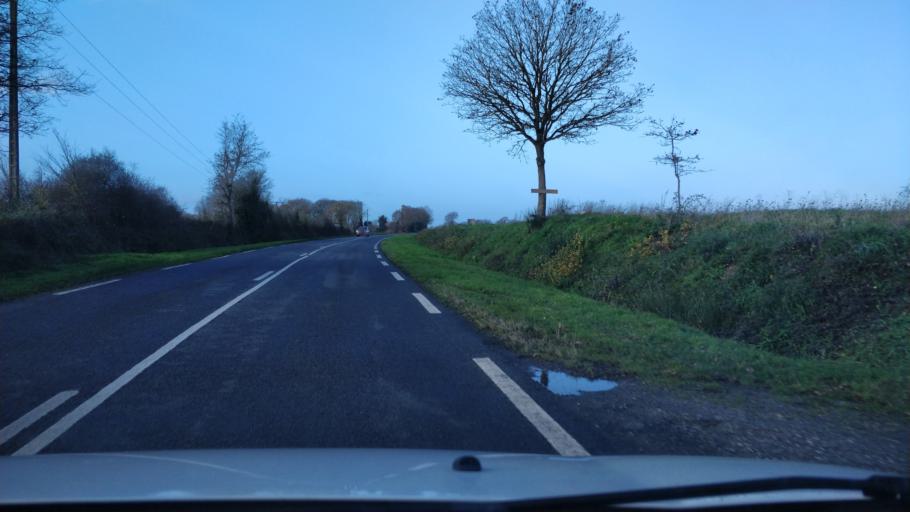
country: FR
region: Pays de la Loire
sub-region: Departement de la Loire-Atlantique
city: Asserac
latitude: 47.4304
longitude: -2.3720
